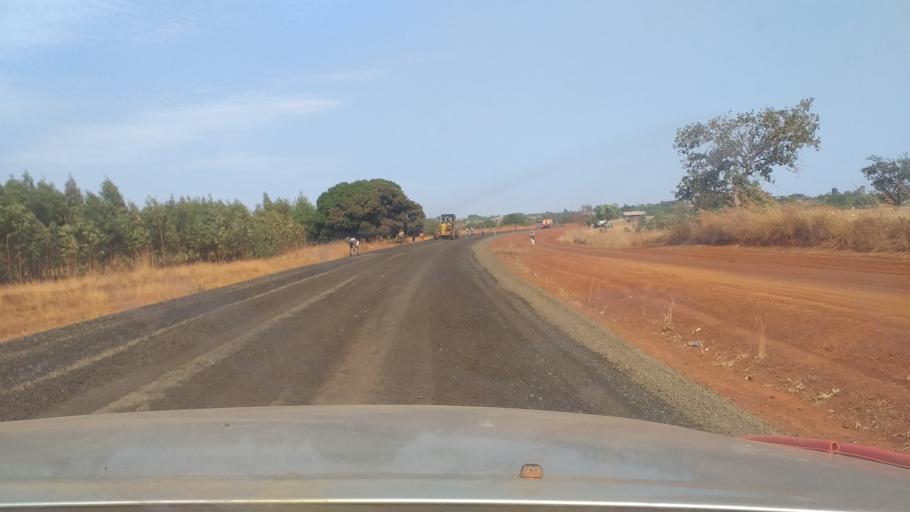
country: ET
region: Binshangul Gumuz
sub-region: Asosa
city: Asosa
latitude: 10.0805
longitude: 34.6201
